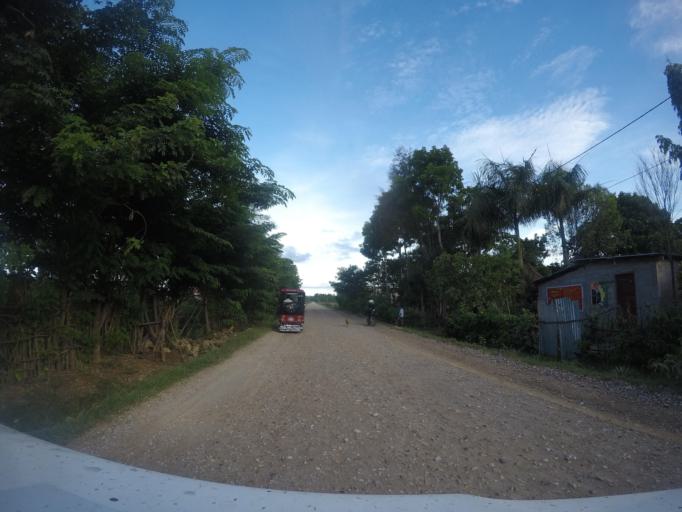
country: TL
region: Lautem
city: Lospalos
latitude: -8.5093
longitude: 126.9979
